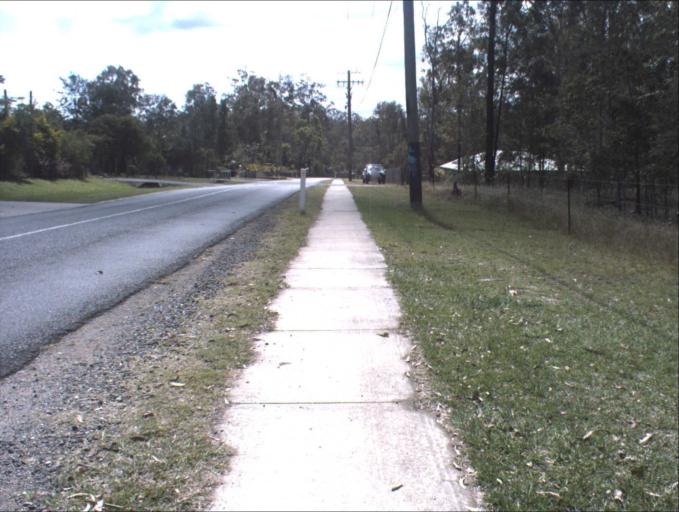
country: AU
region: Queensland
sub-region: Logan
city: North Maclean
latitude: -27.7497
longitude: 153.0144
